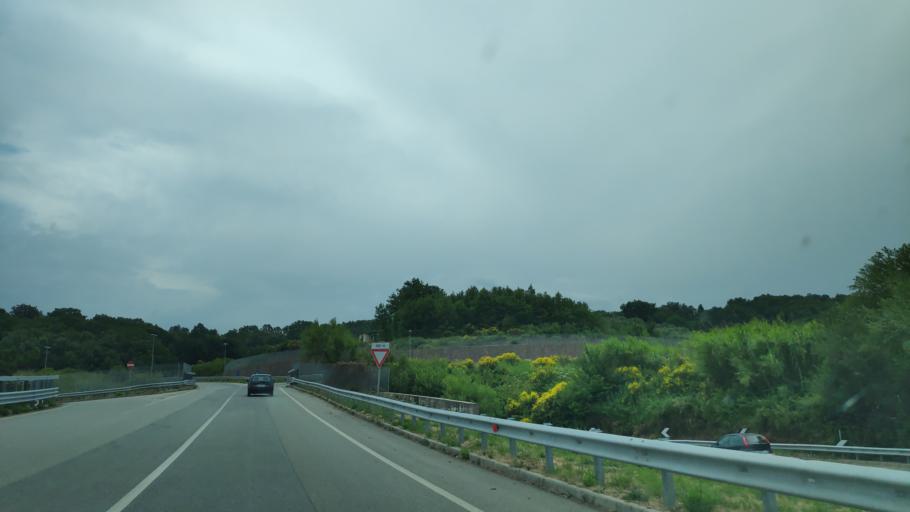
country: IT
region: Calabria
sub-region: Provincia di Catanzaro
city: Argusto
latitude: 38.6814
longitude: 16.4247
